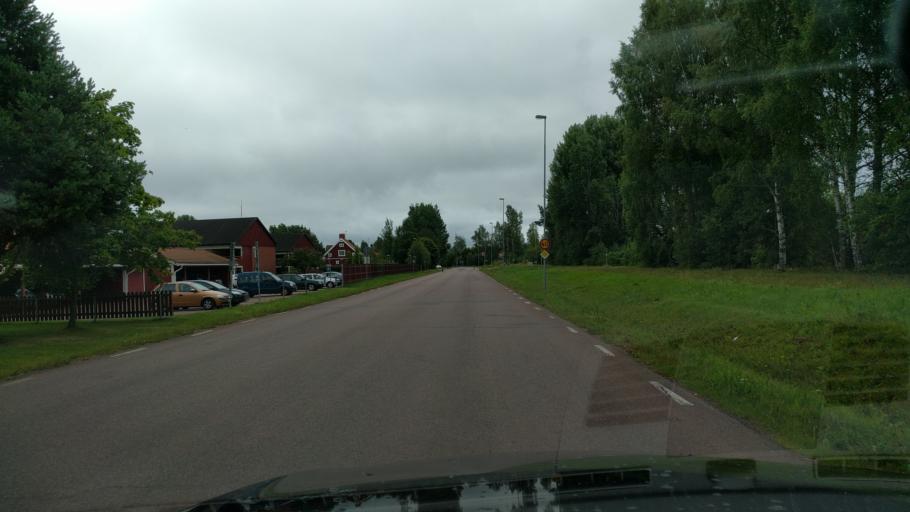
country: SE
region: Dalarna
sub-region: Mora Kommun
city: Mora
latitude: 61.0039
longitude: 14.5270
